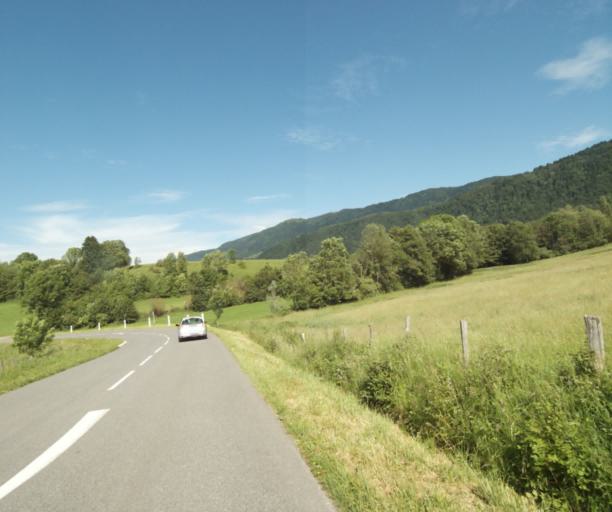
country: FR
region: Rhone-Alpes
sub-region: Departement de la Haute-Savoie
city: Allinges
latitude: 46.3125
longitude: 6.4787
